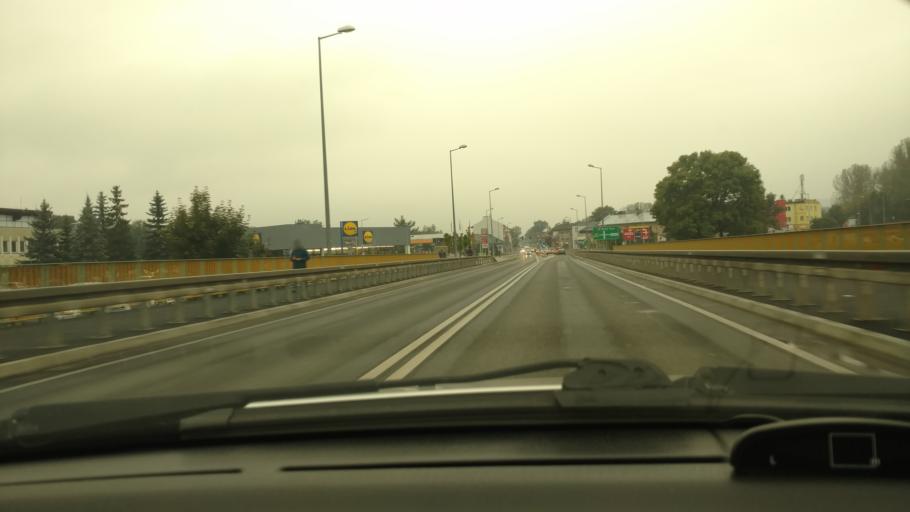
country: PL
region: Lesser Poland Voivodeship
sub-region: Powiat gorlicki
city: Gorlice
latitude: 49.6567
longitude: 21.1622
